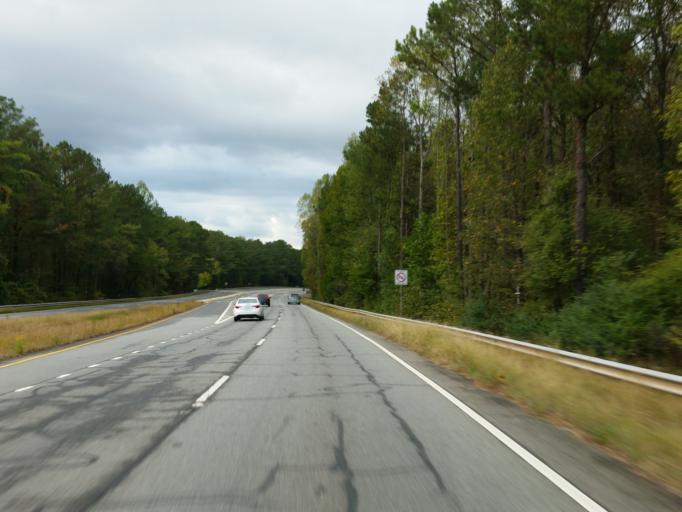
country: US
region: Georgia
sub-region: Bartow County
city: Emerson
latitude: 34.0841
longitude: -84.7330
